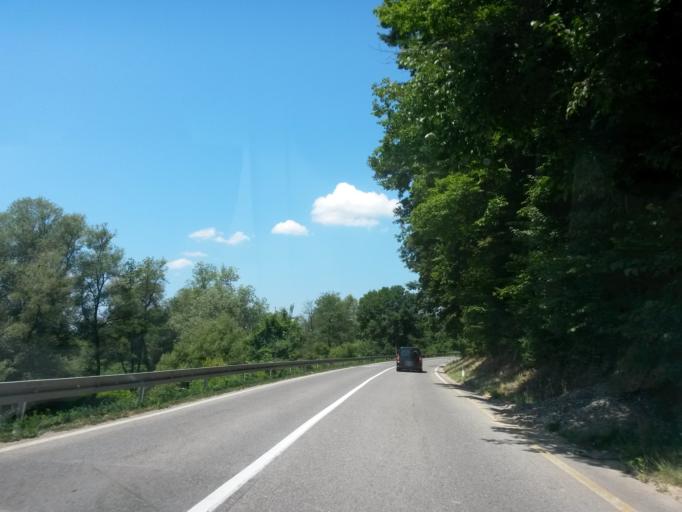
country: BA
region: Federation of Bosnia and Herzegovina
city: Lukavica
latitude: 44.9299
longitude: 18.1577
